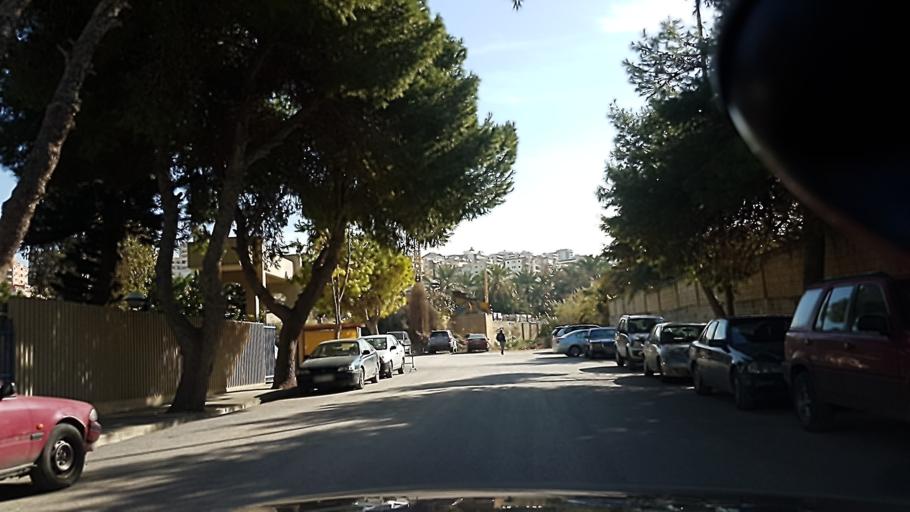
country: LB
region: Liban-Sud
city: Sidon
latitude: 33.5812
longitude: 35.3892
